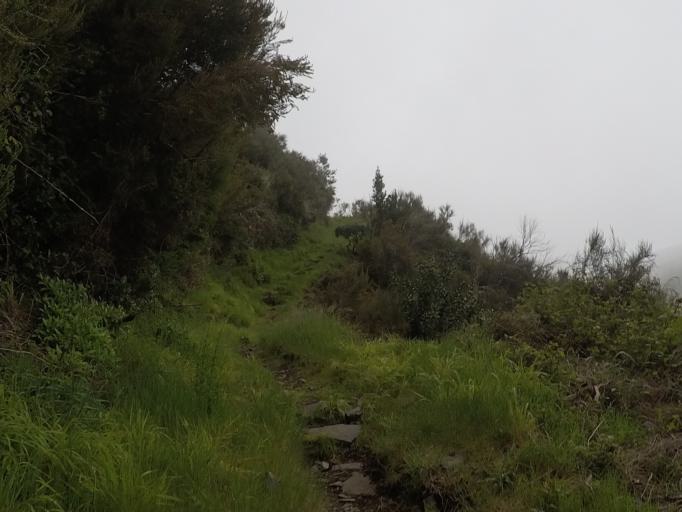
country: PT
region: Madeira
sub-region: Camara de Lobos
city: Curral das Freiras
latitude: 32.7336
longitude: -16.9900
